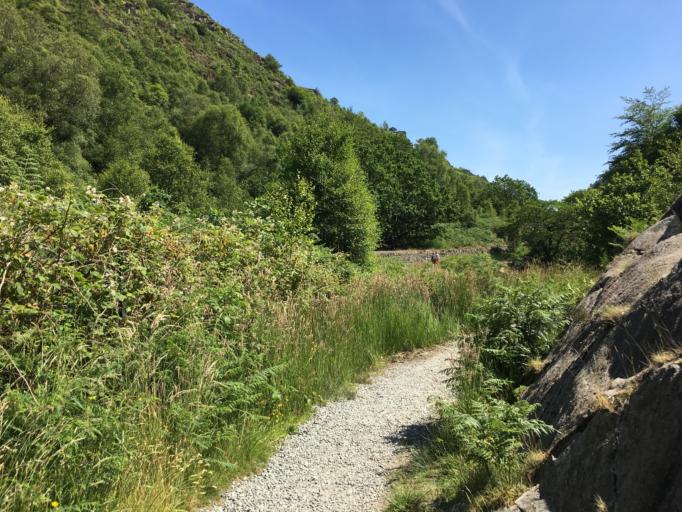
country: GB
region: Wales
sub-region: Gwynedd
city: Penrhyndeudraeth
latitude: 53.0048
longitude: -4.0997
